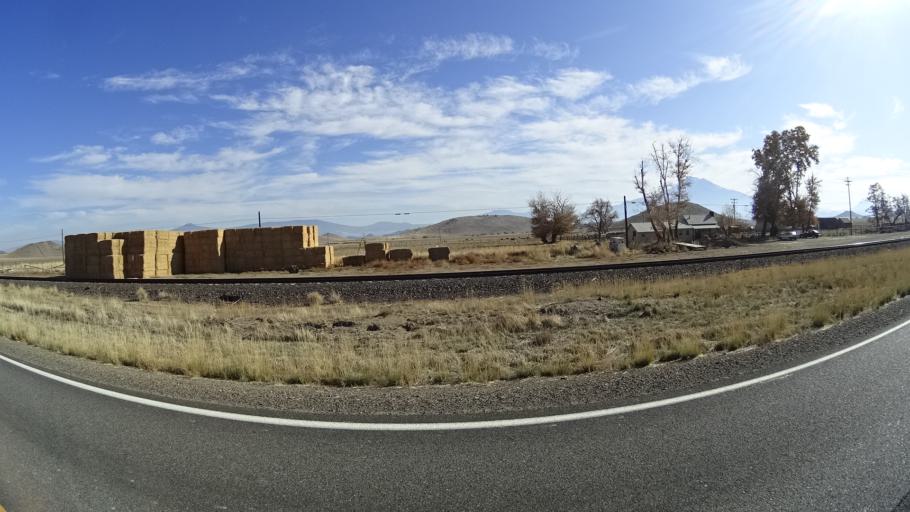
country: US
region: California
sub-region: Siskiyou County
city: Montague
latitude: 41.5446
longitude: -122.5258
